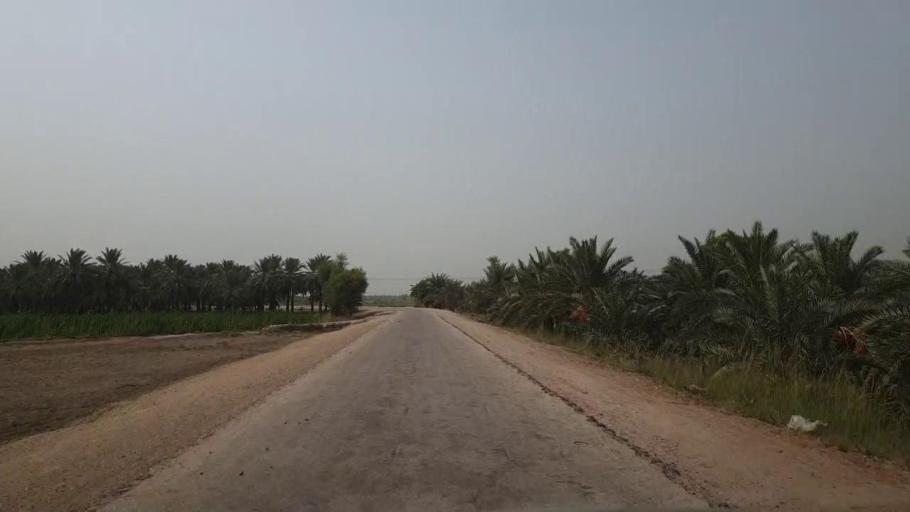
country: PK
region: Sindh
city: Gambat
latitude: 27.4179
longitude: 68.5482
